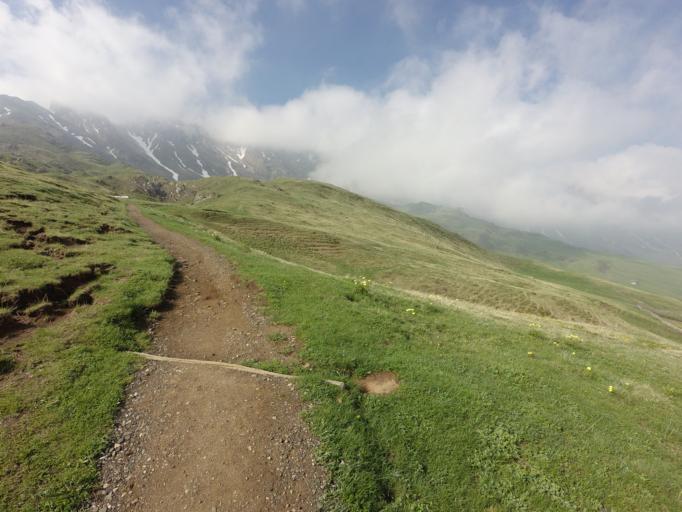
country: IT
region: Trentino-Alto Adige
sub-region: Bolzano
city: Ortisei
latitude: 46.5140
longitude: 11.6346
